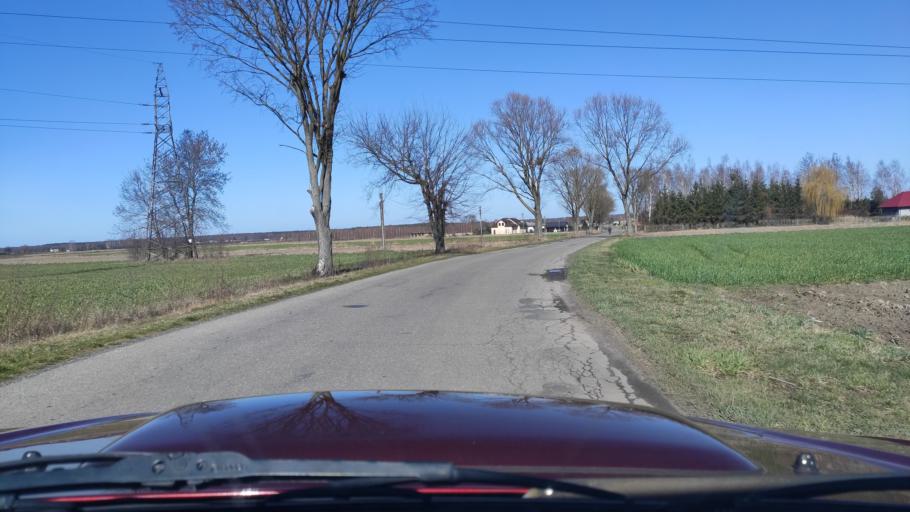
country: PL
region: Masovian Voivodeship
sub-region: Powiat zwolenski
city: Zwolen
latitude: 51.3736
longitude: 21.5822
